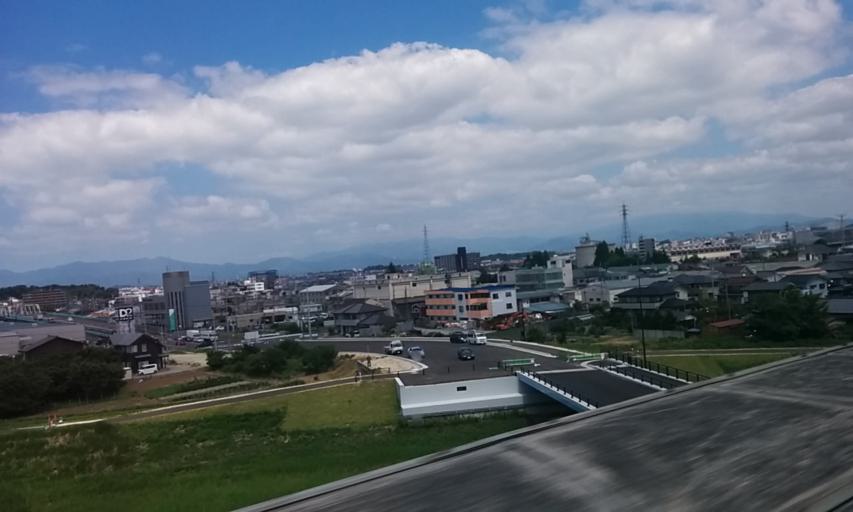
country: JP
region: Fukushima
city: Koriyama
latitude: 37.3588
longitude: 140.3751
